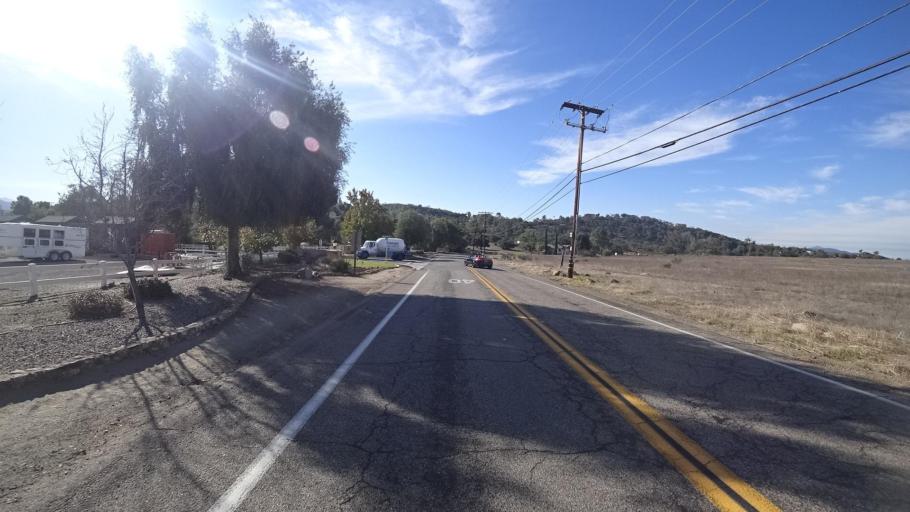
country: US
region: California
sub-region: San Diego County
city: Alpine
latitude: 32.8202
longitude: -116.7584
